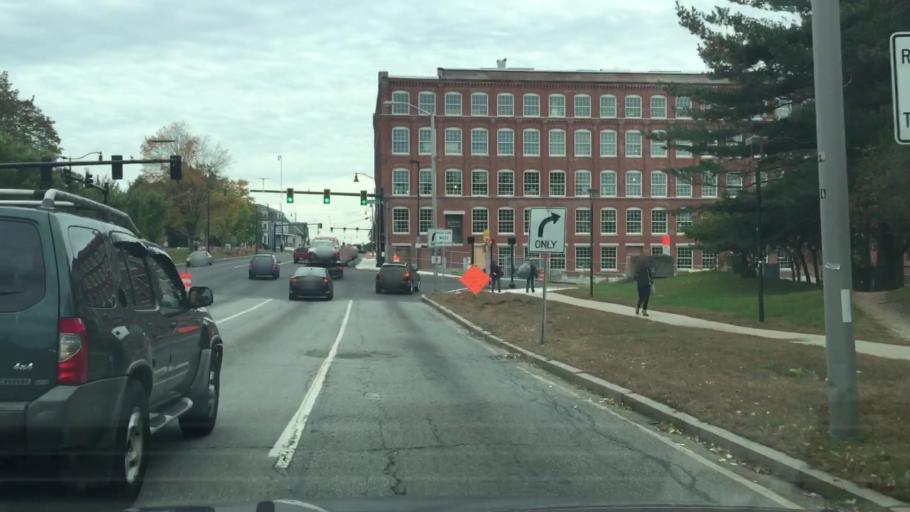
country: US
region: Massachusetts
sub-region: Middlesex County
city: Lowell
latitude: 42.6376
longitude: -71.3141
